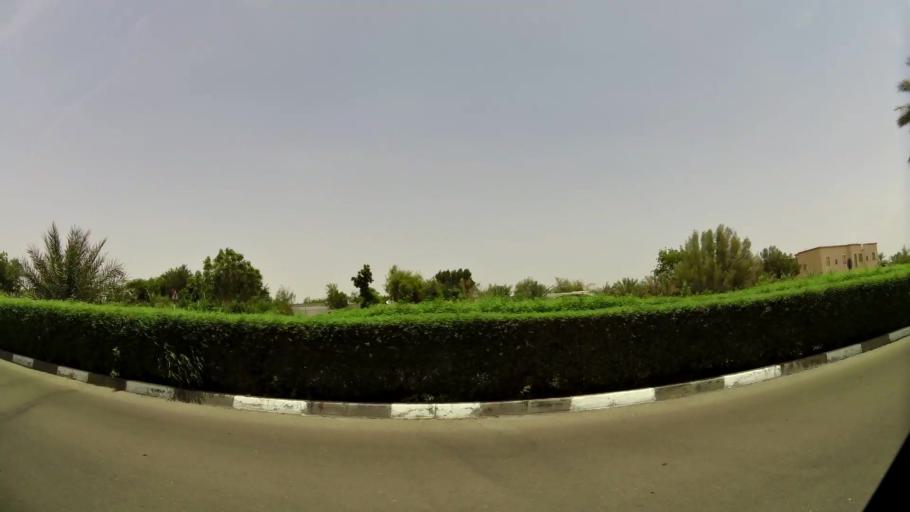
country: AE
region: Abu Dhabi
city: Al Ain
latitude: 24.2176
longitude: 55.7329
